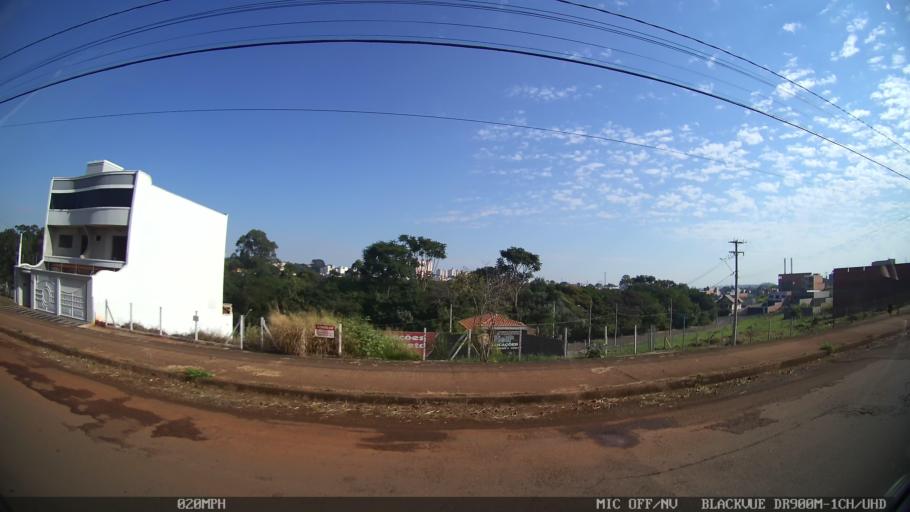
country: BR
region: Sao Paulo
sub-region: Americana
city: Americana
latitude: -22.7277
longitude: -47.3257
